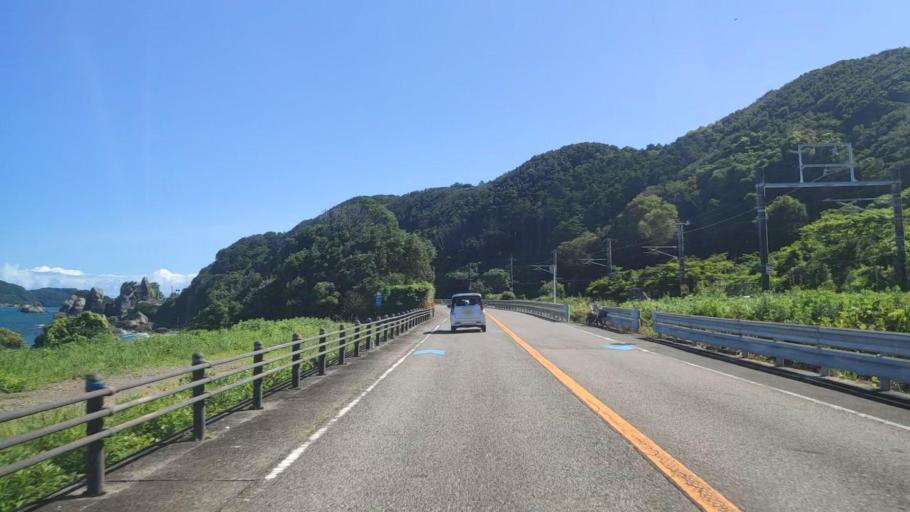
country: JP
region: Wakayama
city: Shingu
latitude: 33.4924
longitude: 135.7947
